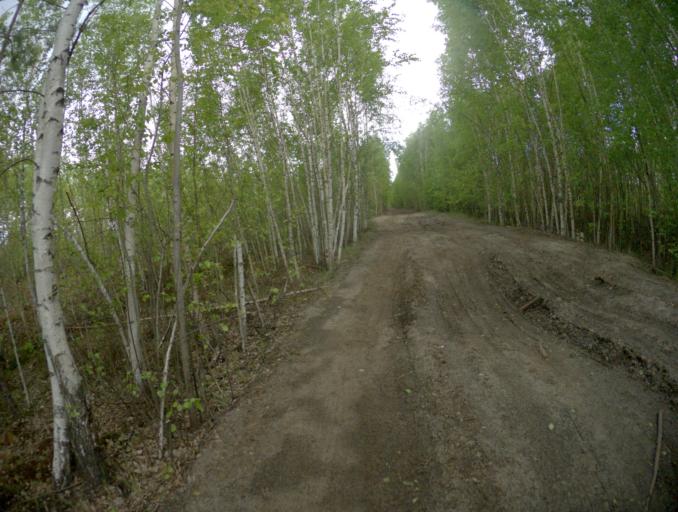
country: RU
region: Moskovskaya
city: Cherusti
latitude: 55.5881
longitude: 40.1194
